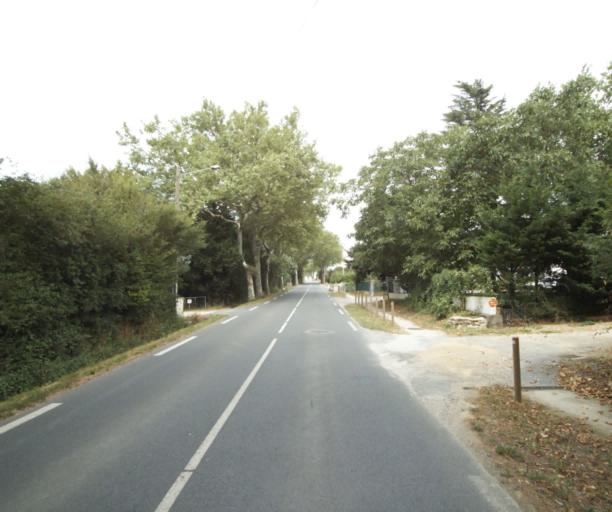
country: FR
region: Midi-Pyrenees
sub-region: Departement du Tarn
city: Soreze
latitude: 43.4548
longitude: 2.0733
